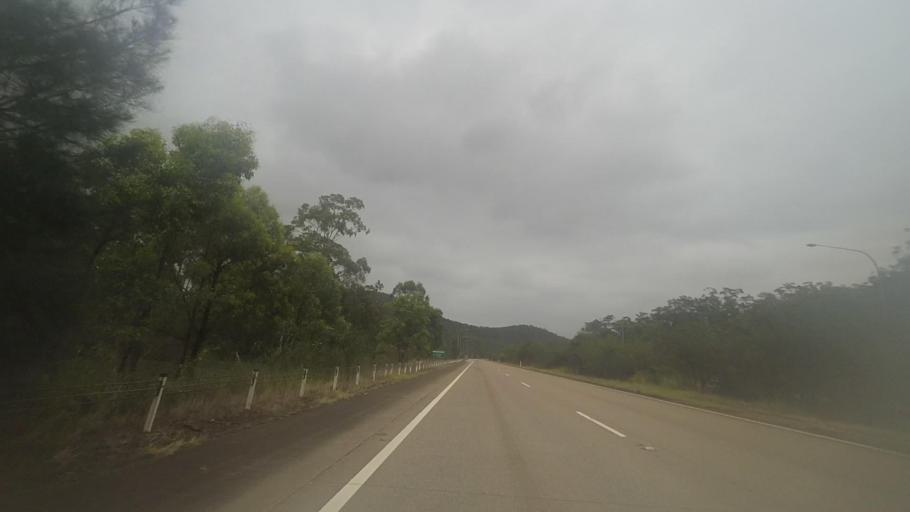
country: AU
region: New South Wales
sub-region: Port Stephens Shire
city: Port Stephens
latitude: -32.6330
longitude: 152.0025
